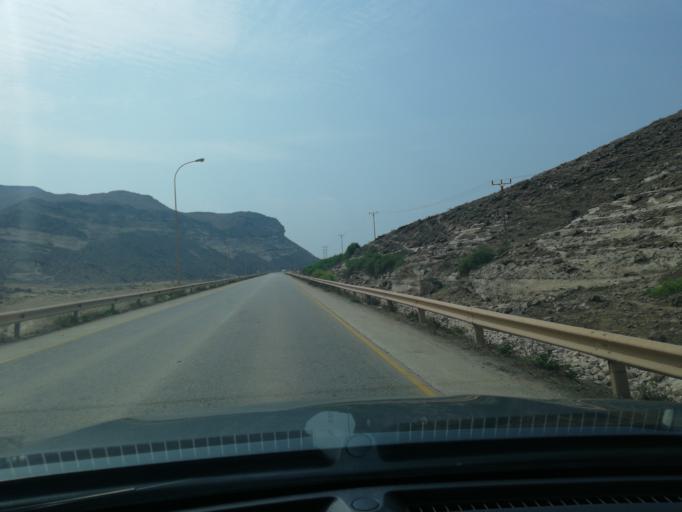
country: OM
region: Zufar
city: Salalah
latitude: 16.8931
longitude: 53.8191
